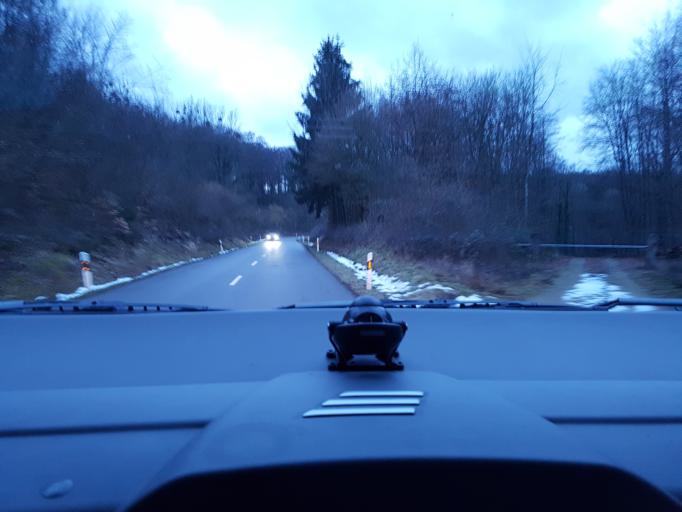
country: LU
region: Grevenmacher
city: Schengen
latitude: 49.4990
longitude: 6.3362
